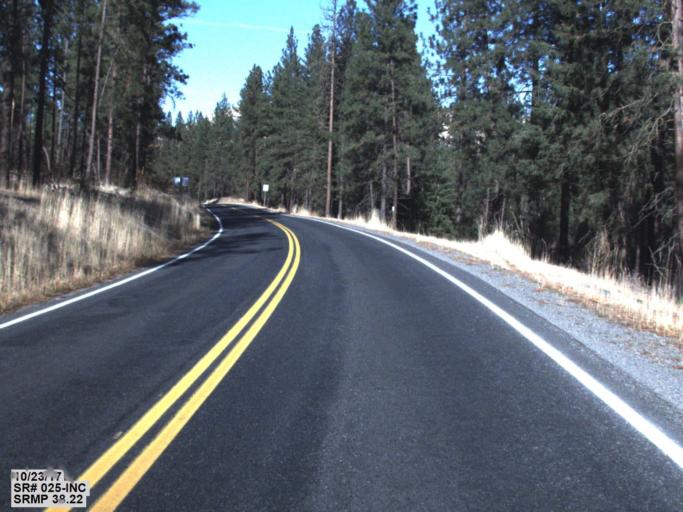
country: US
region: Washington
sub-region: Lincoln County
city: Davenport
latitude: 48.0730
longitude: -118.1971
